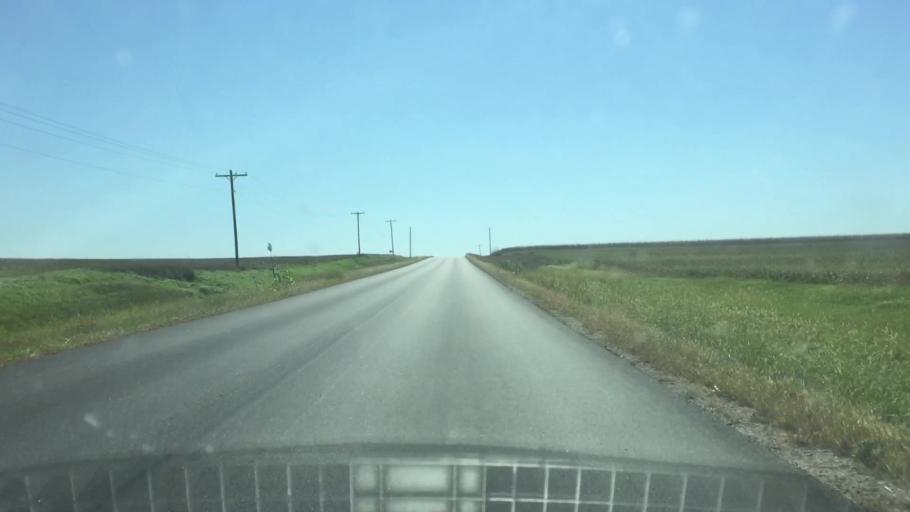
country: US
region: Kansas
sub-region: Marshall County
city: Marysville
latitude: 39.9101
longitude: -96.6009
